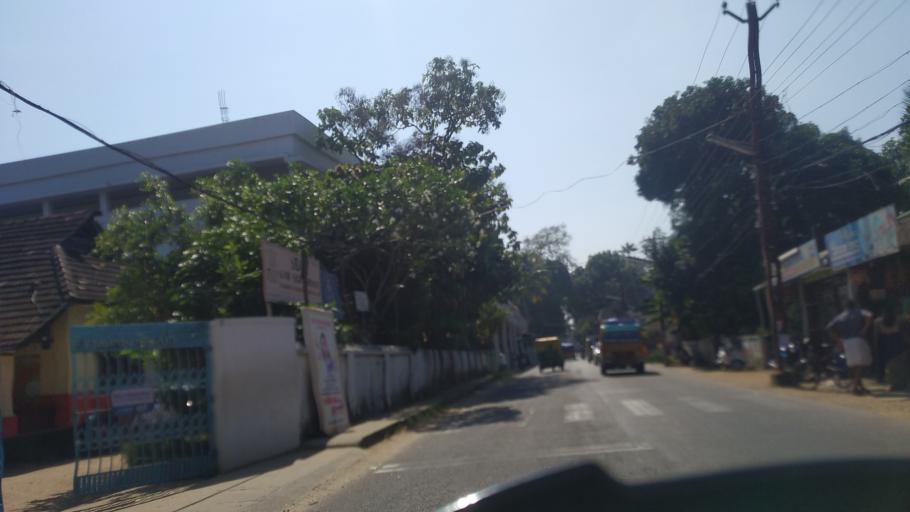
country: IN
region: Kerala
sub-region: Ernakulam
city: Elur
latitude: 10.0853
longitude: 76.2091
